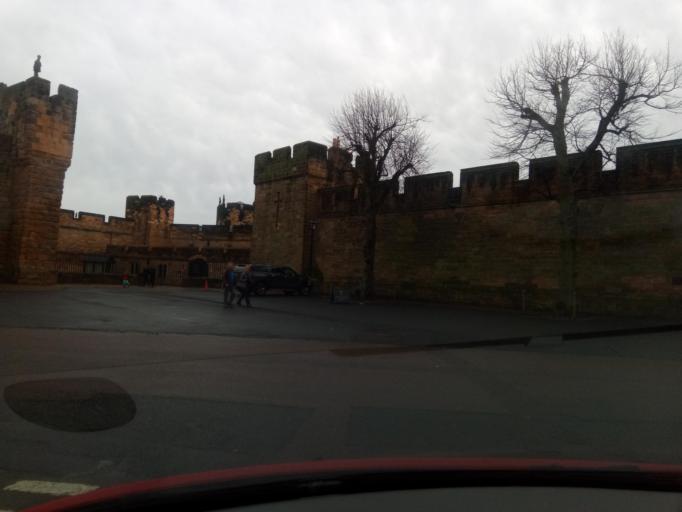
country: GB
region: England
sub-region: Northumberland
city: Alnwick
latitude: 55.4157
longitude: -1.7084
